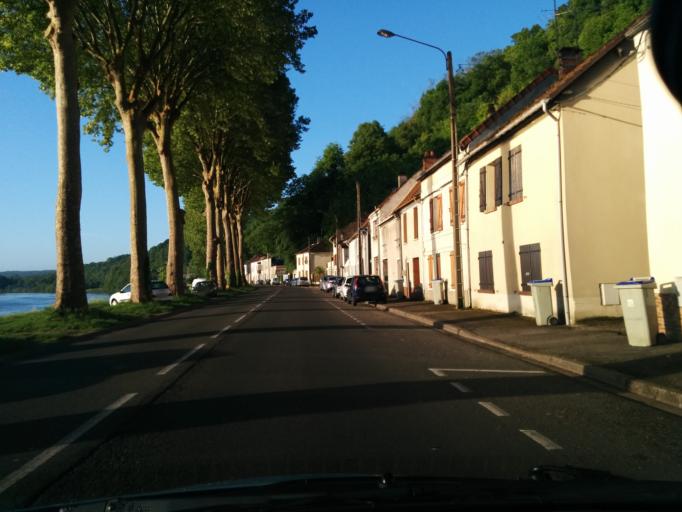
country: FR
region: Ile-de-France
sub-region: Departement des Yvelines
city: Rosny-sur-Seine
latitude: 49.0176
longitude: 1.6107
